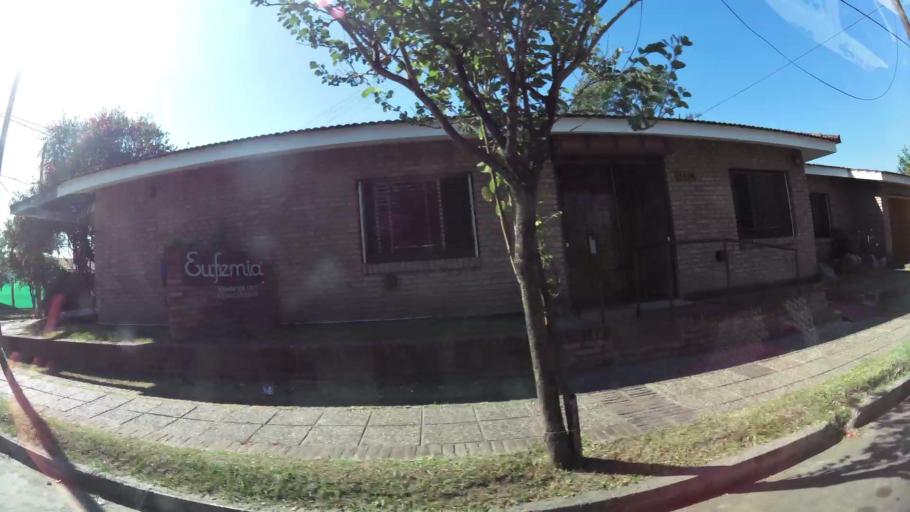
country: AR
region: Cordoba
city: Villa Allende
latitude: -31.3501
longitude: -64.2463
